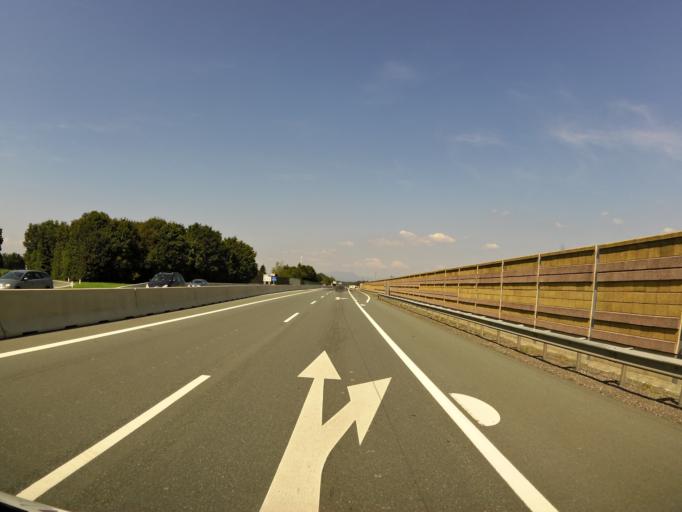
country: AT
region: Styria
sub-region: Politischer Bezirk Leibnitz
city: Weitendorf
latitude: 46.8924
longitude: 15.4722
